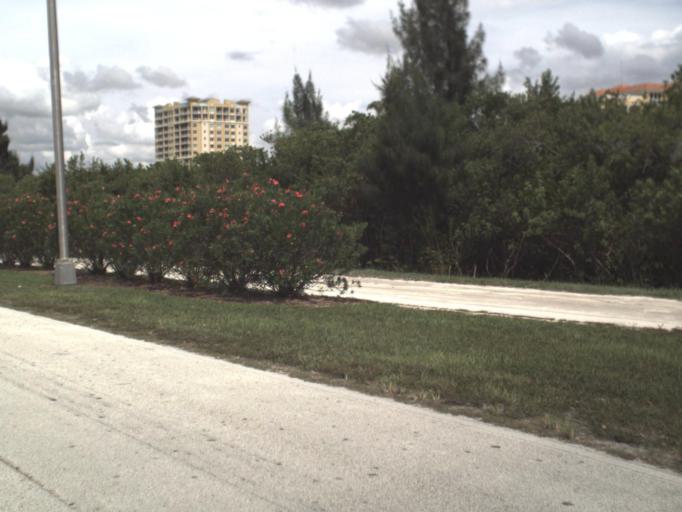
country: US
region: Florida
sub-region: Manatee County
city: Bradenton
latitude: 27.5089
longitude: -82.5630
